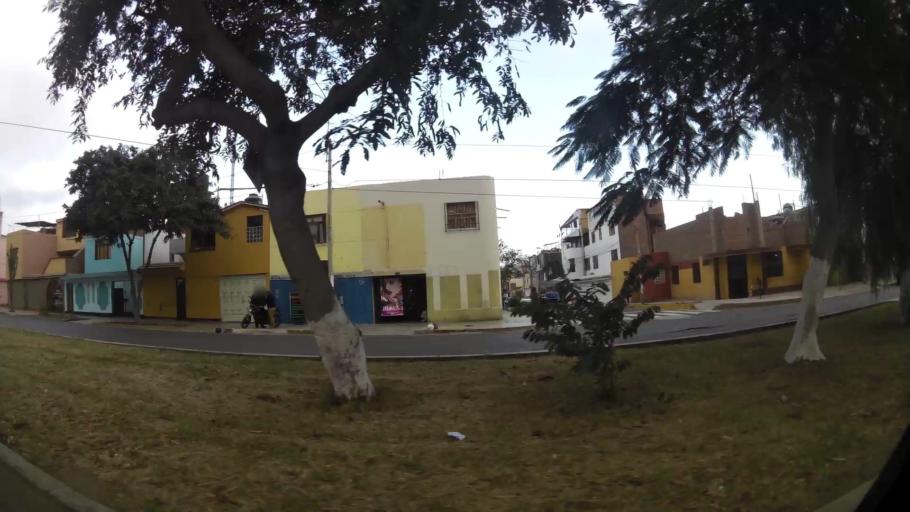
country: PE
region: La Libertad
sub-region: Provincia de Trujillo
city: La Esperanza
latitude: -8.0929
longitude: -79.0359
